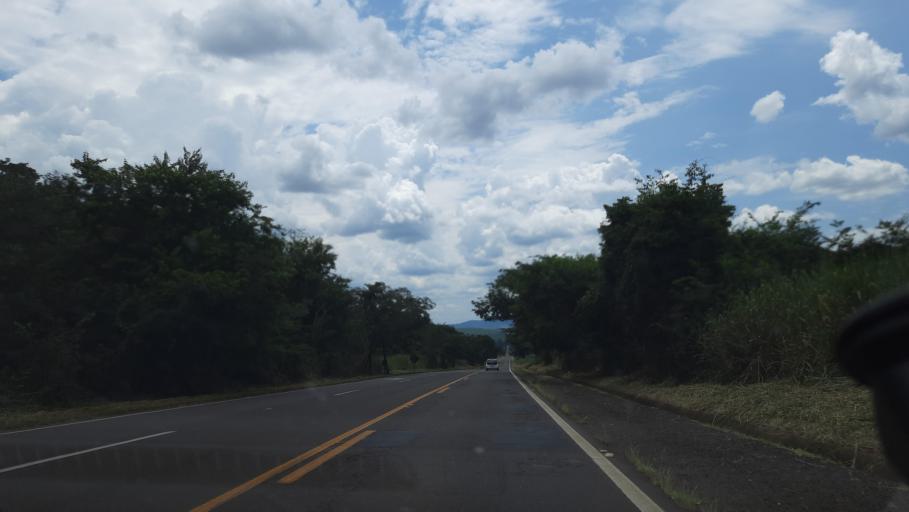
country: BR
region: Sao Paulo
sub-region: Mococa
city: Mococa
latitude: -21.4874
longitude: -47.0795
